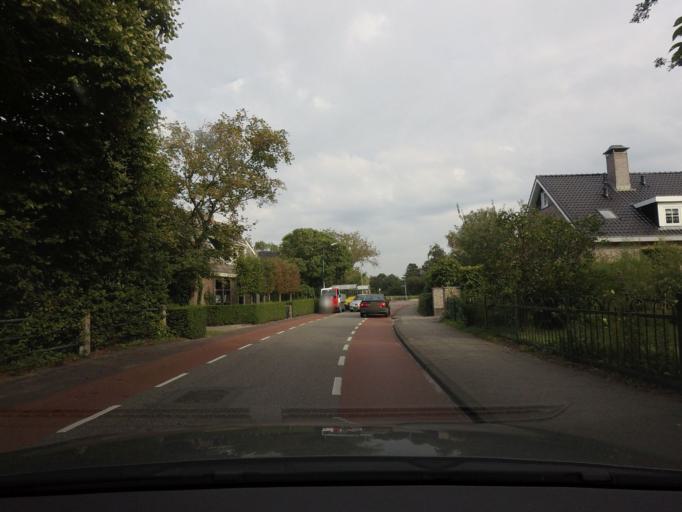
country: NL
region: North Holland
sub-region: Gemeente Schagen
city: Harenkarspel
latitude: 52.7212
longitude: 4.6706
